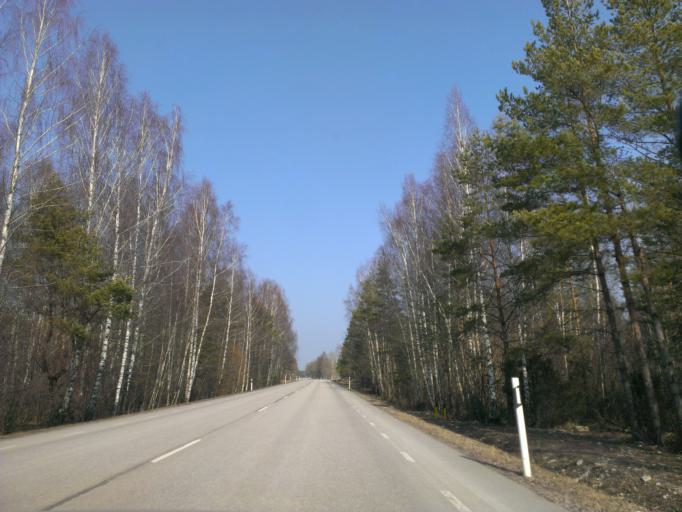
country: EE
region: Saare
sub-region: Orissaare vald
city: Orissaare
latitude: 58.5442
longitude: 23.0551
